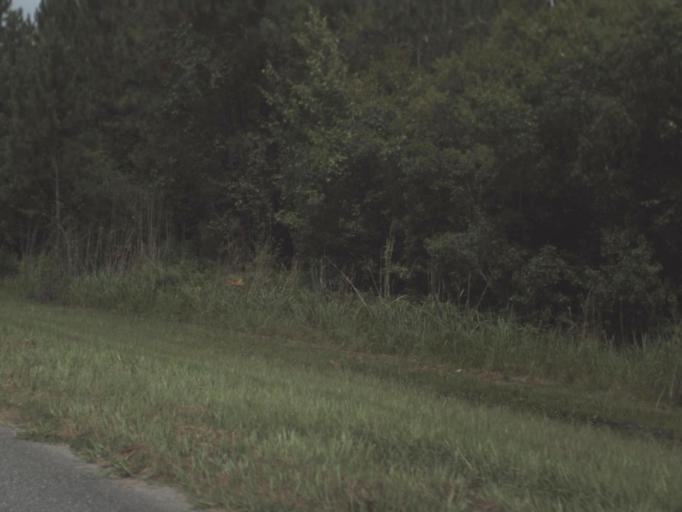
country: US
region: Florida
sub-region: Baker County
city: Macclenny
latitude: 30.1335
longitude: -82.1956
